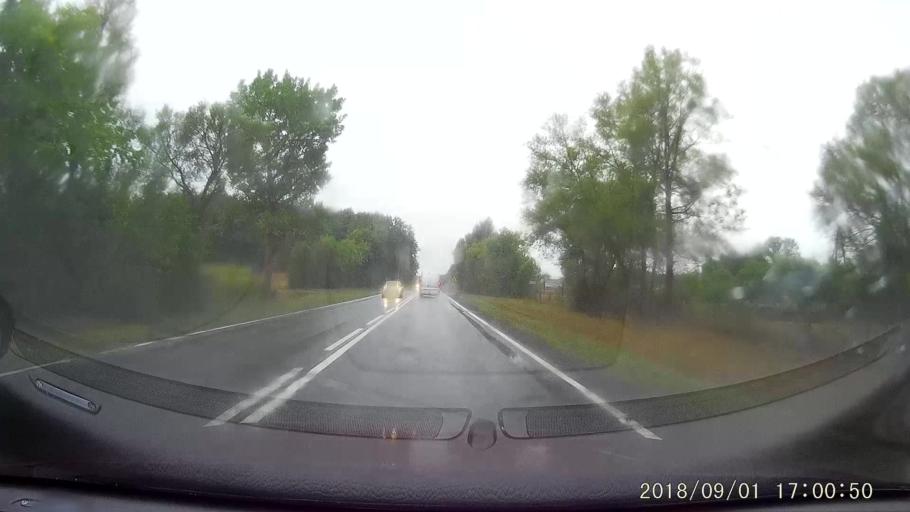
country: PL
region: Lubusz
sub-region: Powiat zielonogorski
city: Swidnica
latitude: 51.8977
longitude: 15.4012
